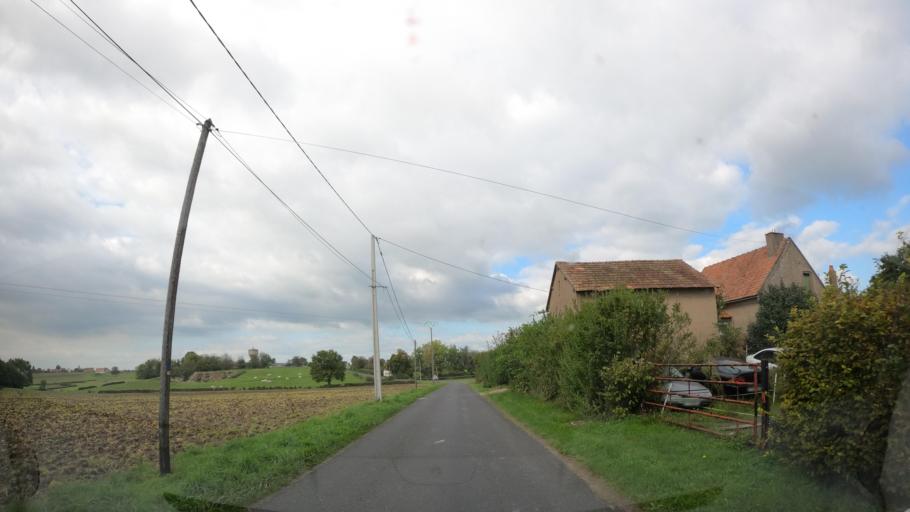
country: FR
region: Auvergne
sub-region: Departement de l'Allier
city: Lapalisse
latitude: 46.3494
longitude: 3.6248
